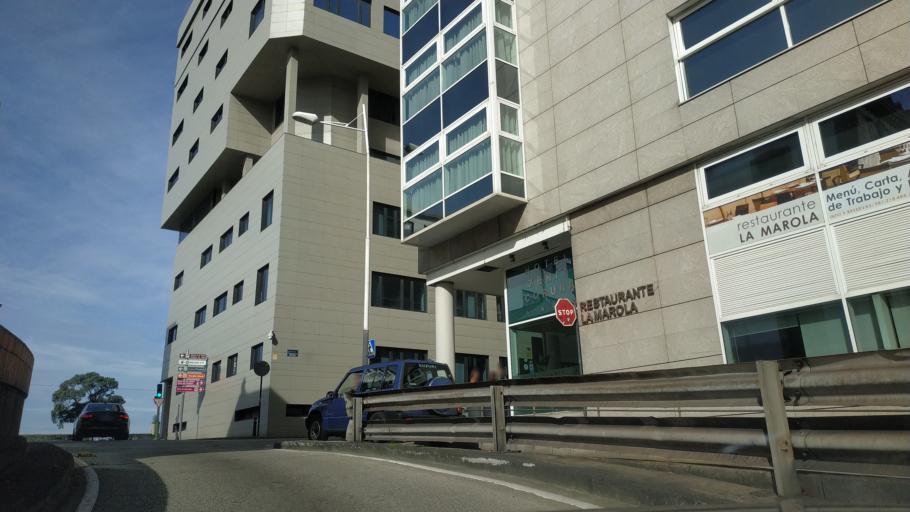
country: ES
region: Galicia
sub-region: Provincia da Coruna
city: A Coruna
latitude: 43.3685
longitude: -8.4066
